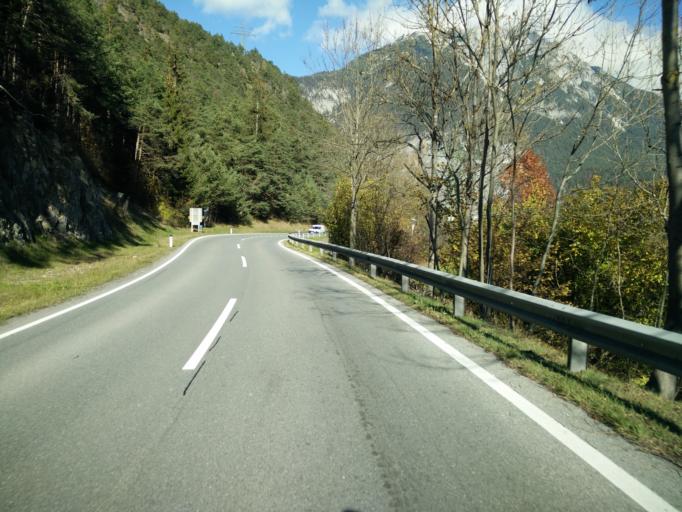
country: AT
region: Tyrol
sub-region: Politischer Bezirk Imst
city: Nassereith
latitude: 47.3022
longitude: 10.8355
